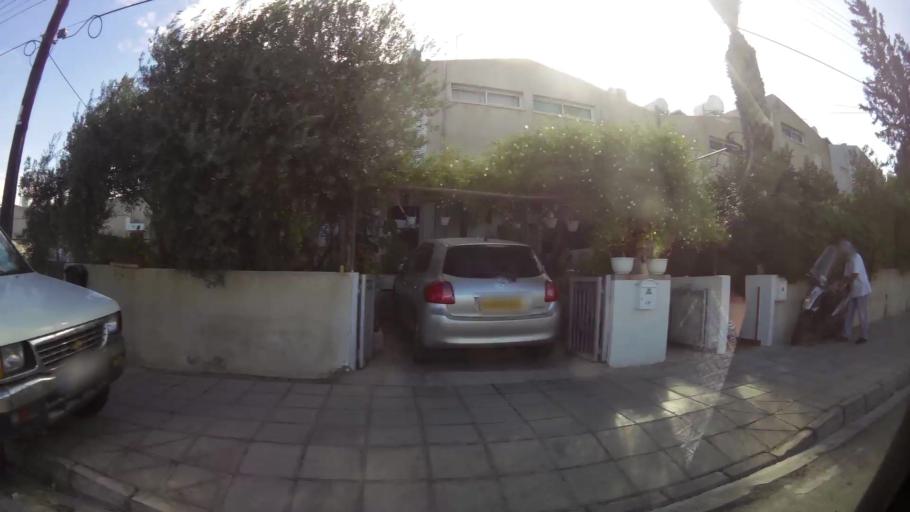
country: CY
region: Lefkosia
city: Nicosia
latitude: 35.1277
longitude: 33.3470
